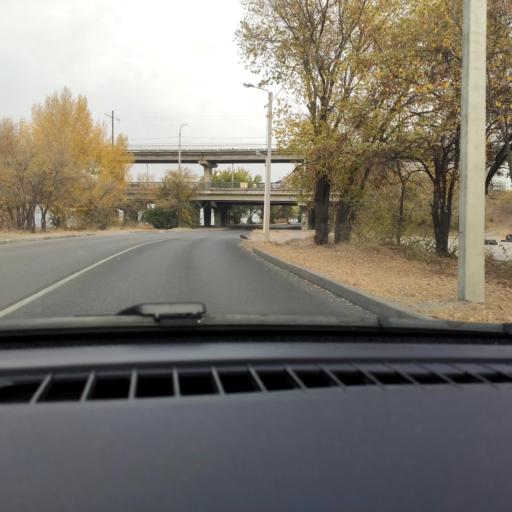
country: RU
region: Voronezj
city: Voronezh
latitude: 51.6885
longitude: 39.2489
